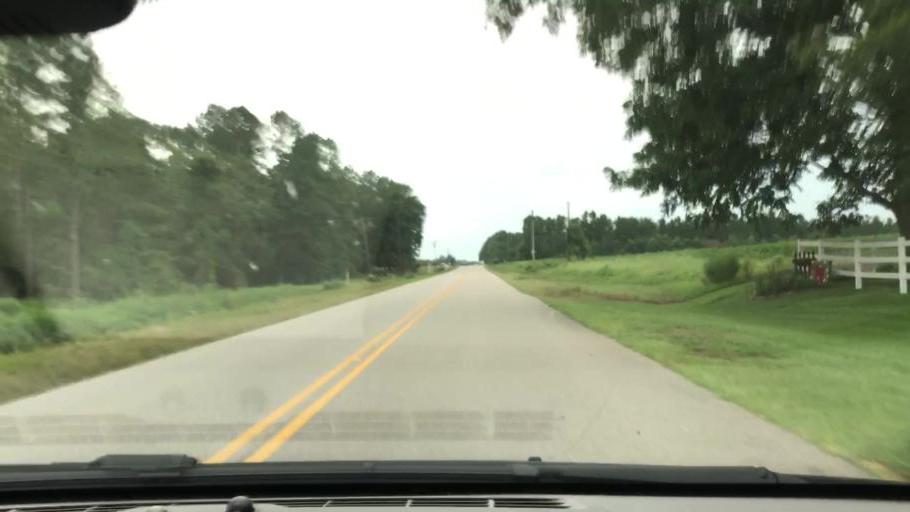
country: US
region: Alabama
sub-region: Houston County
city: Ashford
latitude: 31.2632
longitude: -85.1667
